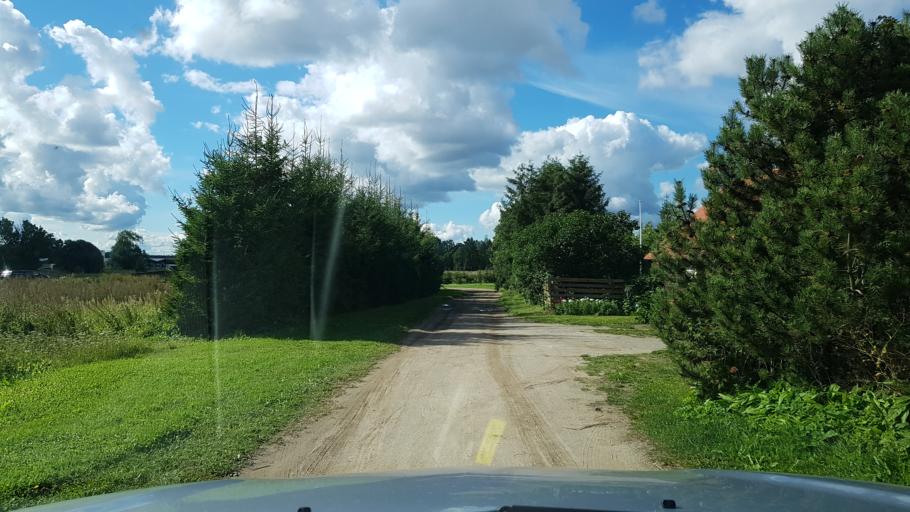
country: EE
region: Harju
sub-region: Tallinna linn
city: Tallinn
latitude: 59.3833
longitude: 24.7995
